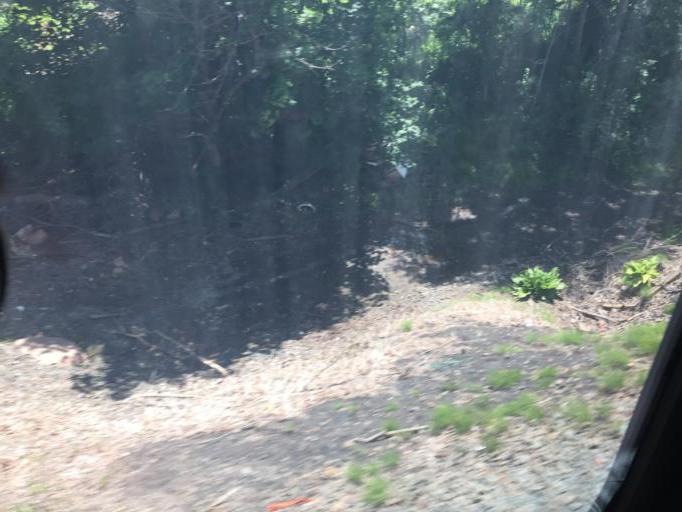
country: US
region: Connecticut
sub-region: New Haven County
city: Meriden
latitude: 41.5123
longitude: -72.8141
